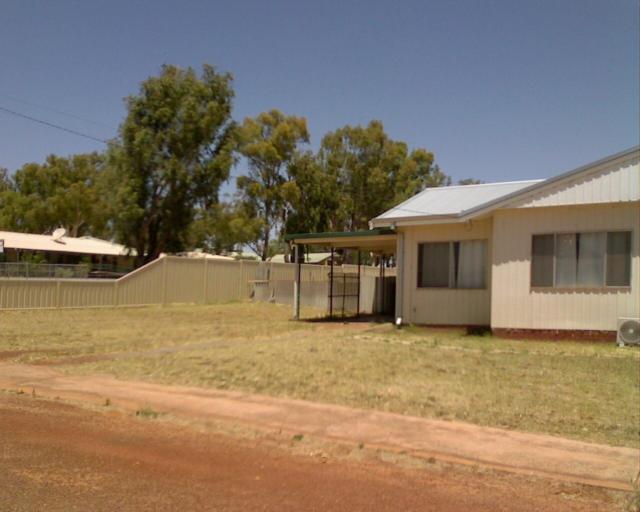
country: AU
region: Western Australia
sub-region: Irwin
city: Dongara
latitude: -29.1937
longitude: 115.4421
